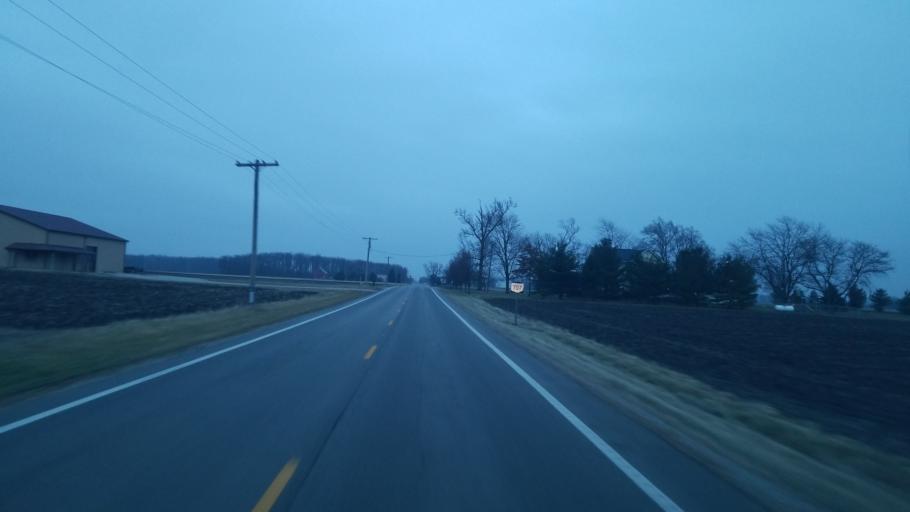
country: US
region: Ohio
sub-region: Mercer County
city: Rockford
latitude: 40.6551
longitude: -84.6056
